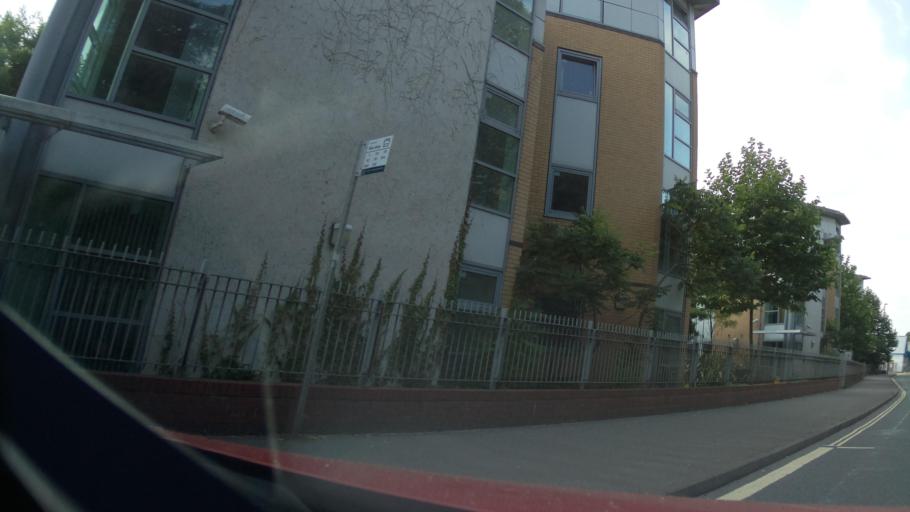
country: GB
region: England
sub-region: Devon
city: Exeter
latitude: 50.7394
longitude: -3.5454
